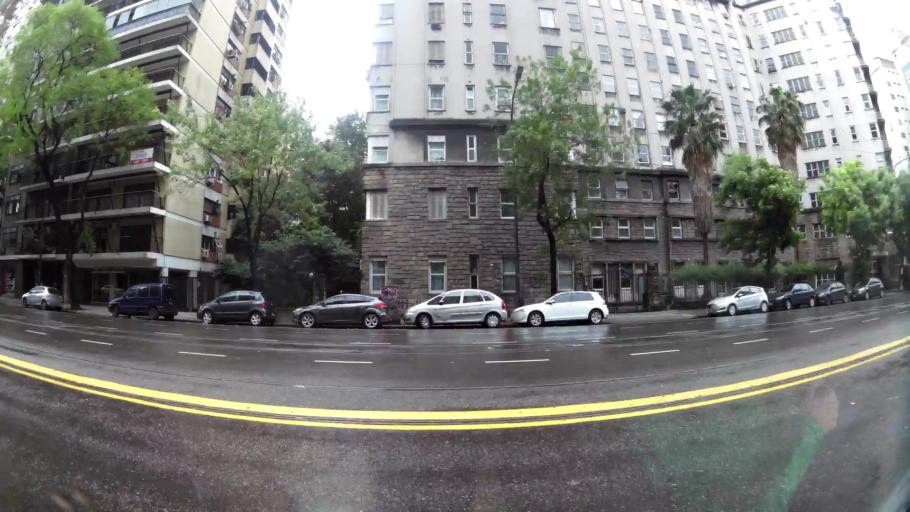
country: AR
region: Buenos Aires F.D.
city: Retiro
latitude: -34.5819
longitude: -58.4133
